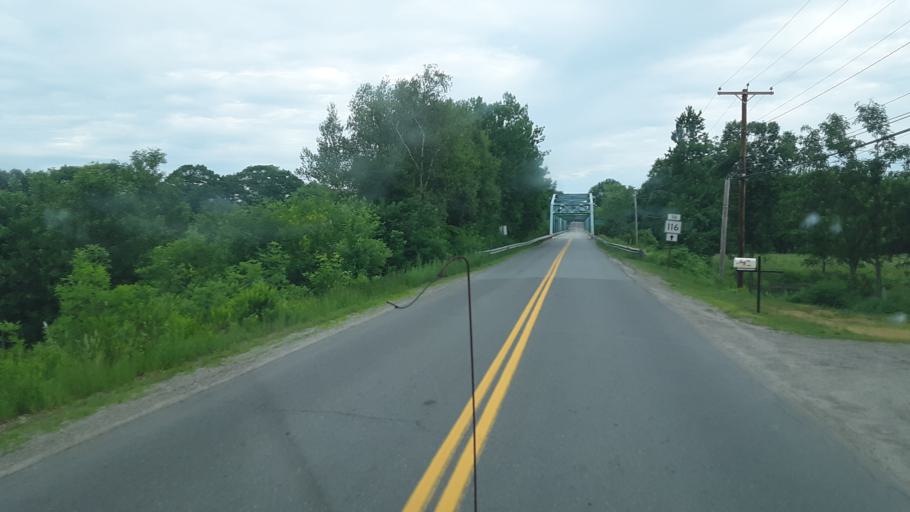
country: US
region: Maine
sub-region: Penobscot County
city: Lincoln
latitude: 45.4309
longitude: -68.4576
